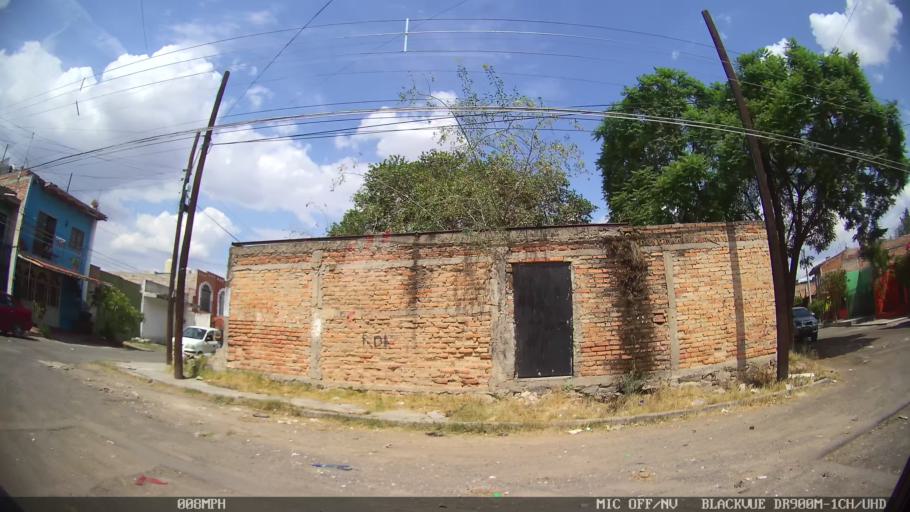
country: MX
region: Jalisco
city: Tonala
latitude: 20.6252
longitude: -103.2645
